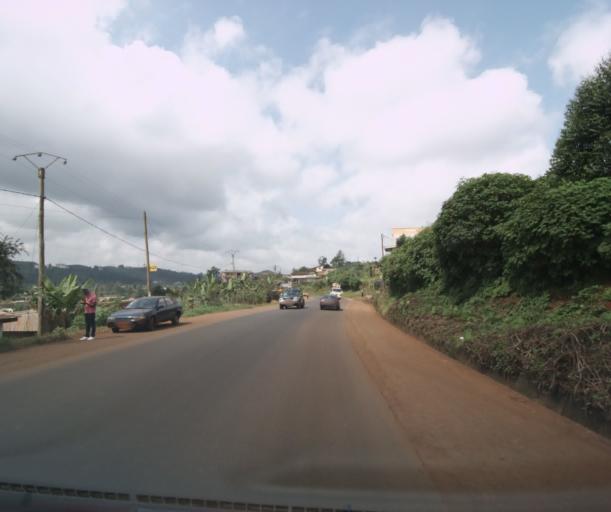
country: CM
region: West
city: Dschang
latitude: 5.4574
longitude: 10.0691
